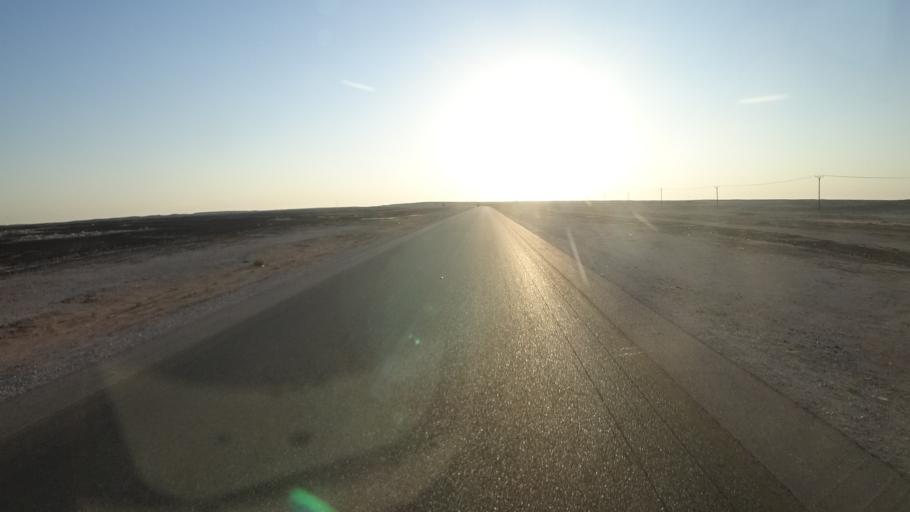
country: OM
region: Zufar
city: Salalah
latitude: 17.5558
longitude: 53.4365
